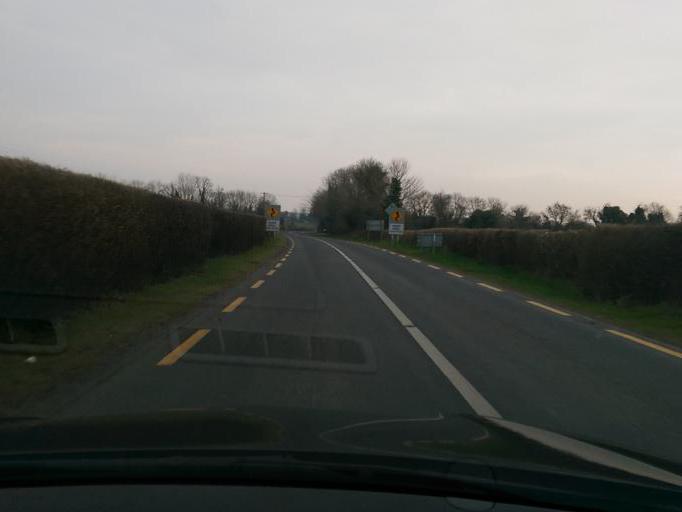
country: IE
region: Leinster
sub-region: An Longfort
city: Ballymahon
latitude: 53.5282
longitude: -7.7939
